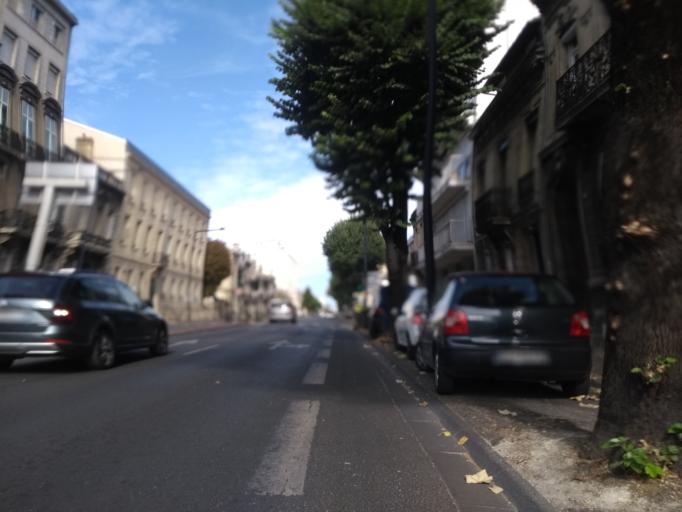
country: FR
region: Aquitaine
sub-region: Departement de la Gironde
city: Le Bouscat
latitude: 44.8495
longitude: -0.5965
